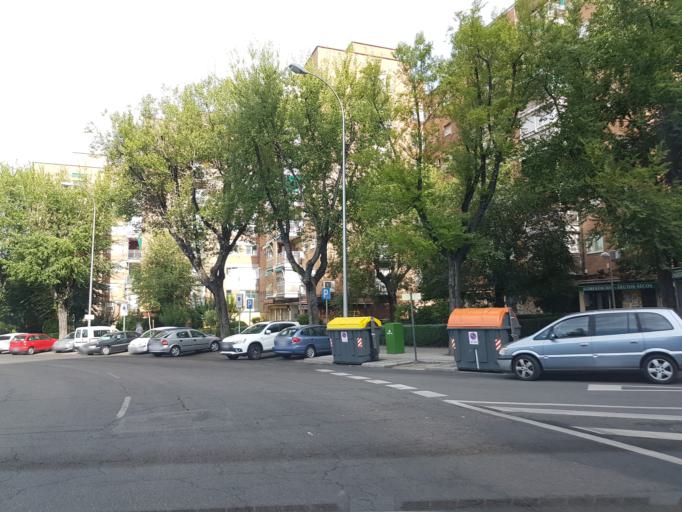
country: ES
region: Madrid
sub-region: Provincia de Madrid
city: Moratalaz
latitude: 40.4073
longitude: -3.6582
